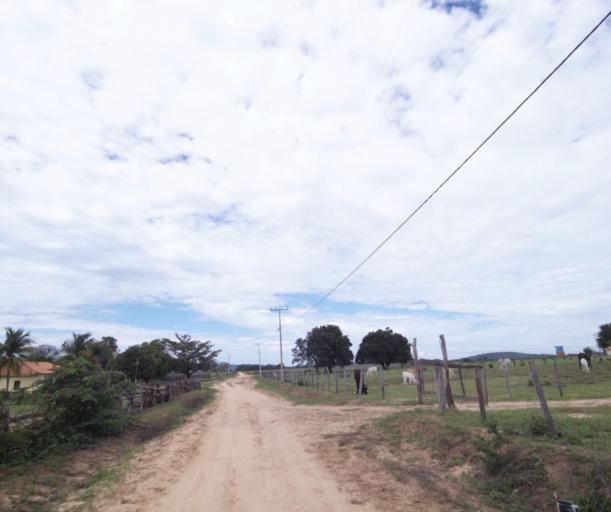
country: BR
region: Bahia
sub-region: Carinhanha
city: Carinhanha
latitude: -14.2509
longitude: -44.3520
